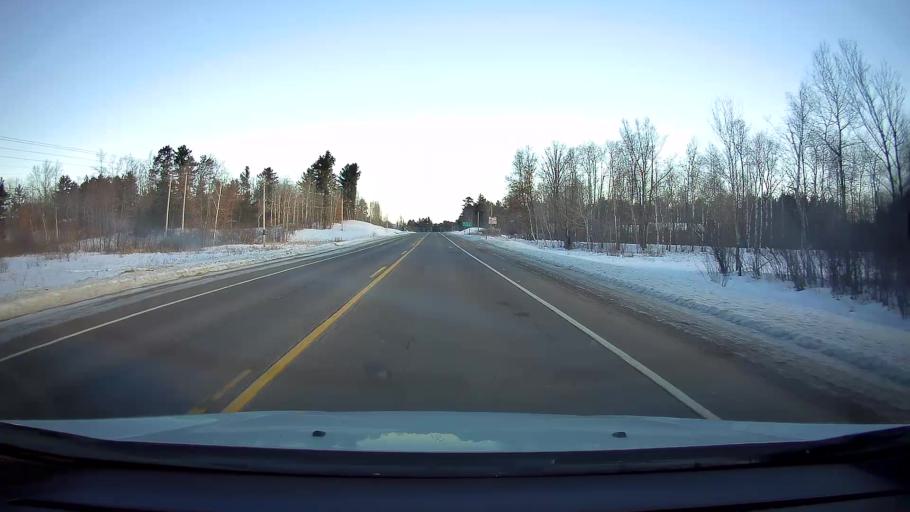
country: US
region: Wisconsin
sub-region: Barron County
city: Cumberland
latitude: 45.5938
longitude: -92.0177
